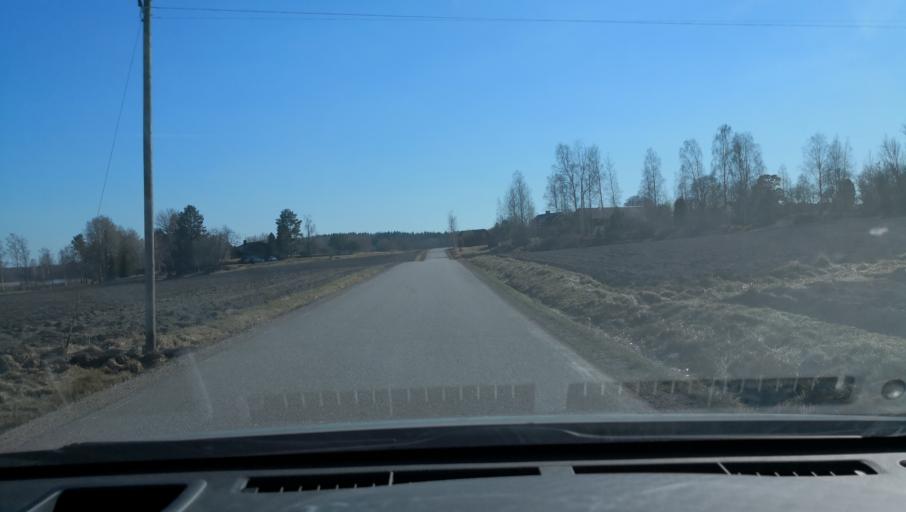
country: SE
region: Vaestmanland
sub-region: Sala Kommun
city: Sala
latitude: 60.0805
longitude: 16.4964
